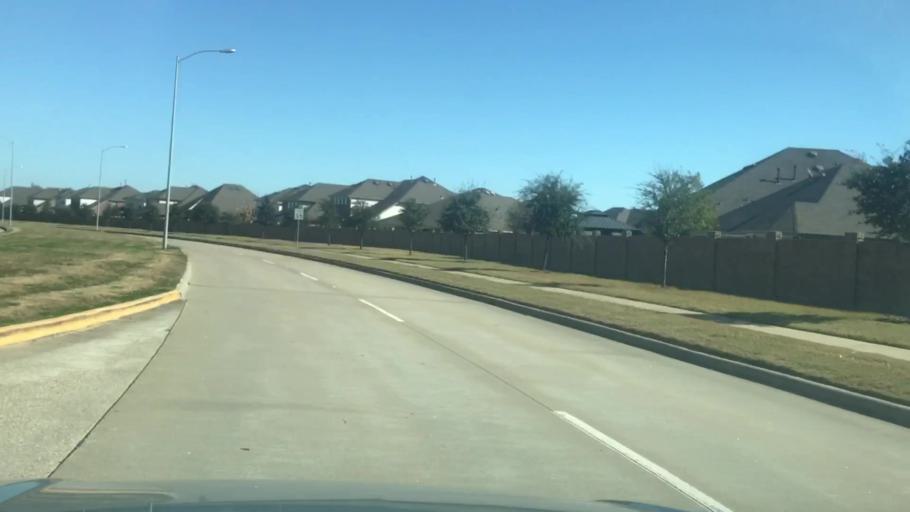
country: US
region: Texas
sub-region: Fort Bend County
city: Cinco Ranch
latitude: 29.7344
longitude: -95.8047
